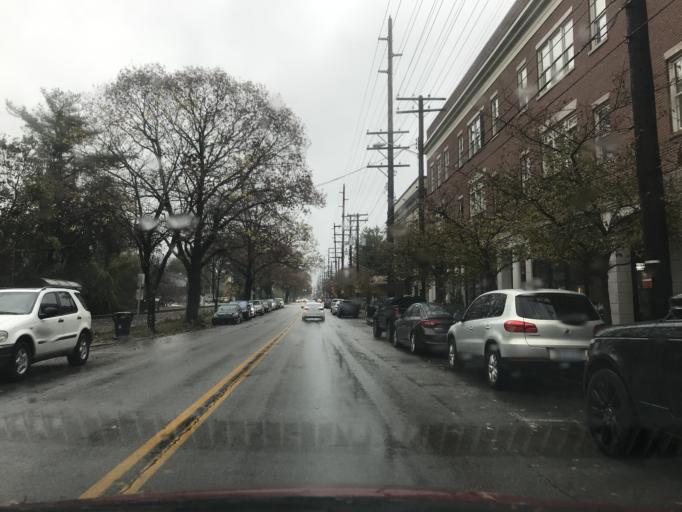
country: US
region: Kentucky
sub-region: Jefferson County
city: Indian Hills
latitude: 38.2546
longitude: -85.6882
